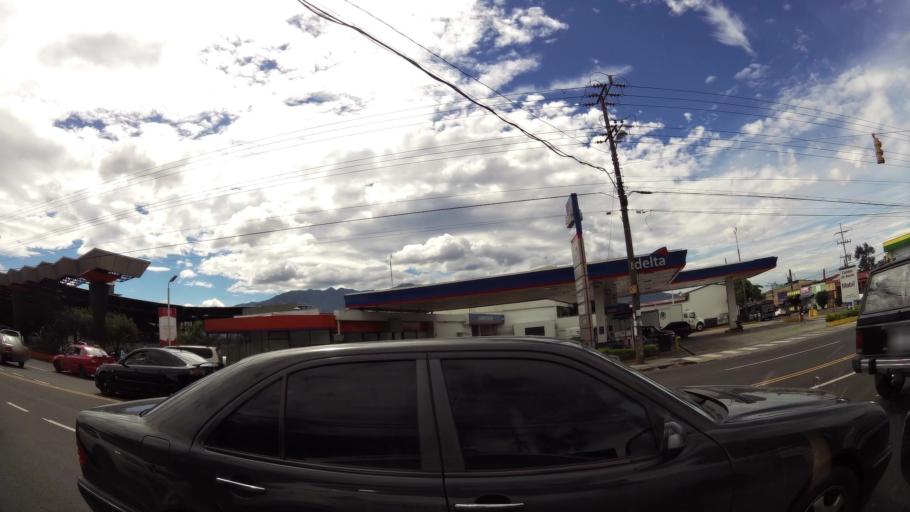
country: CR
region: San Jose
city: San Jose
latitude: 9.9182
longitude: -84.0705
